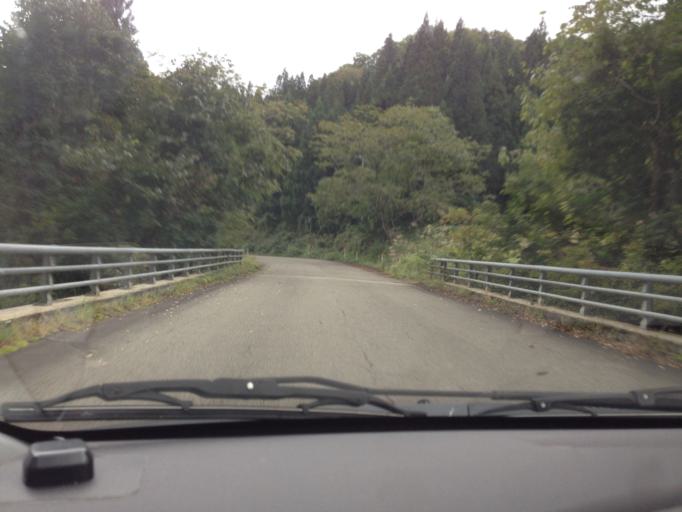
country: JP
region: Fukushima
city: Kitakata
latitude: 37.4417
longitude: 139.6511
